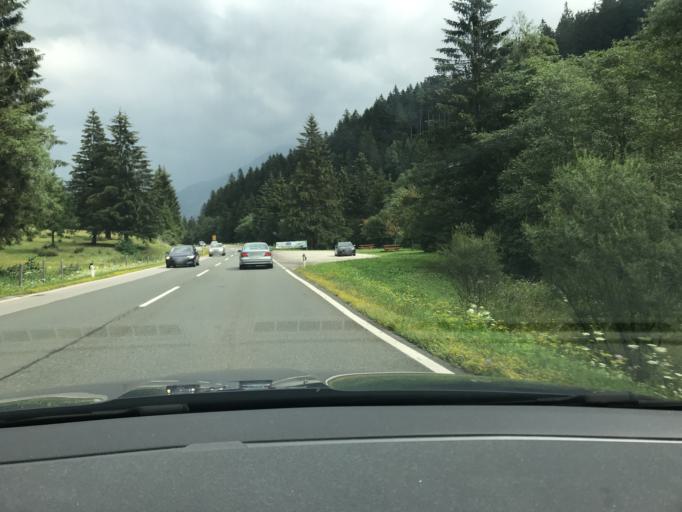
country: AT
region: Tyrol
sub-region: Politischer Bezirk Lienz
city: Matrei in Osttirol
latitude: 46.9647
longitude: 12.5516
